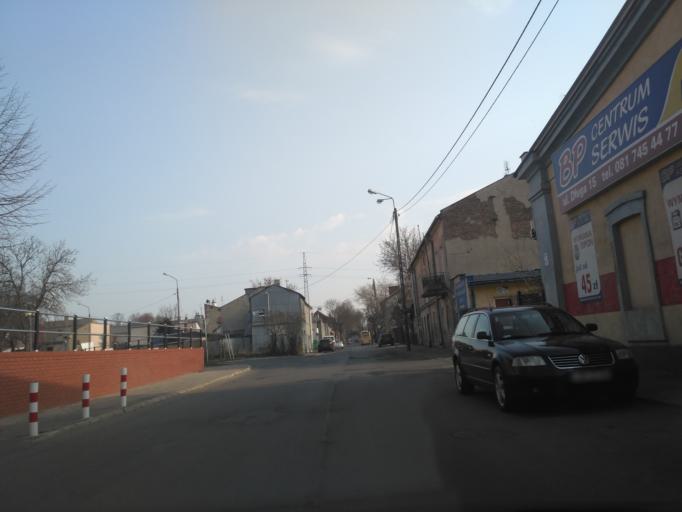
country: PL
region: Lublin Voivodeship
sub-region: Powiat lubelski
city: Lublin
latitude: 51.2322
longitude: 22.5783
